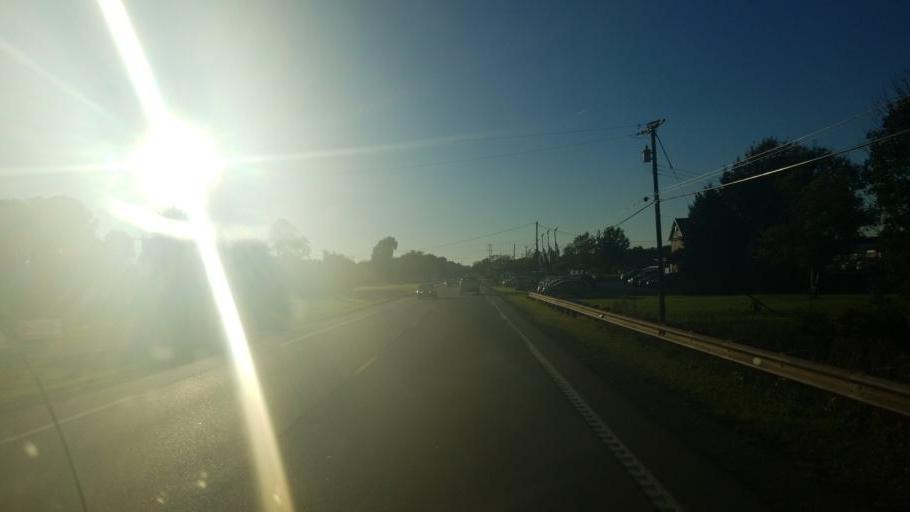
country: US
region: Ohio
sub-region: Stark County
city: Alliance
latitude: 40.9015
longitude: -81.0668
